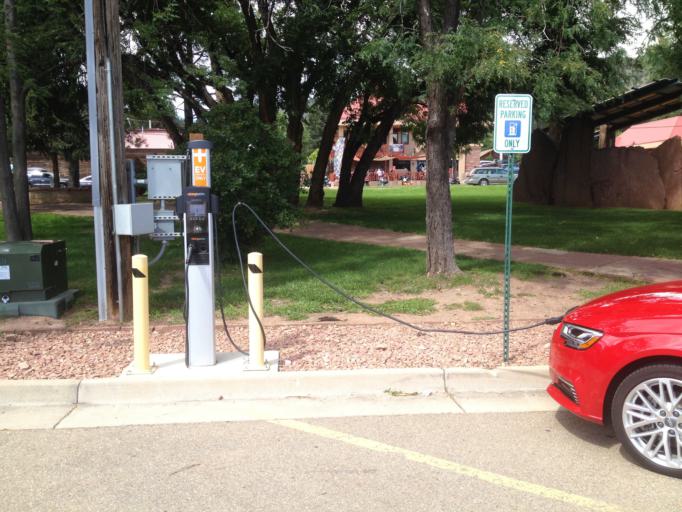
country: US
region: Colorado
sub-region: Boulder County
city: Lyons
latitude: 40.2236
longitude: -105.2688
